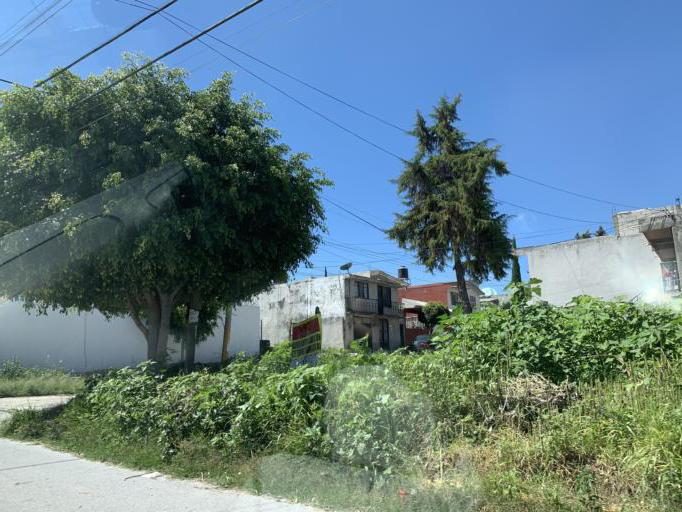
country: MX
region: Puebla
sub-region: Puebla
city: El Capulo (La Quebradora)
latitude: 18.9644
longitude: -98.2643
